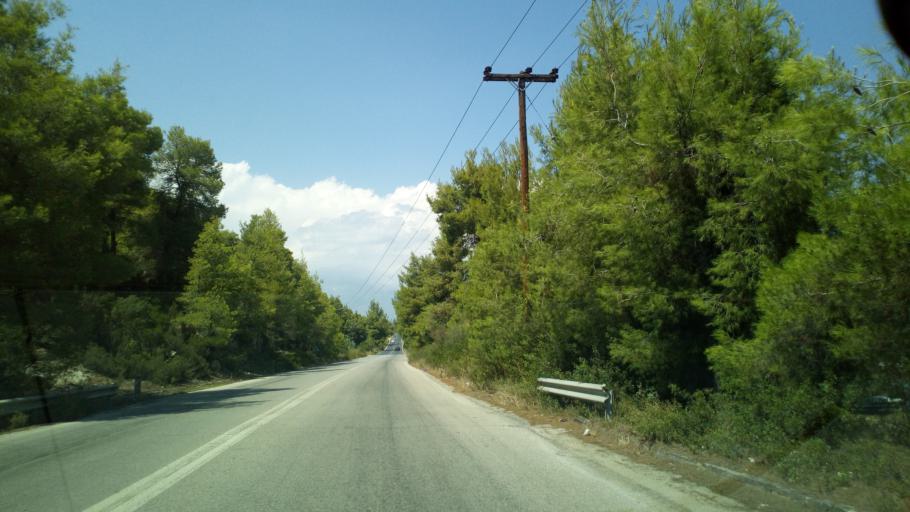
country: GR
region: Central Macedonia
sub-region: Nomos Chalkidikis
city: Agios Nikolaos
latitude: 40.2024
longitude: 23.7629
